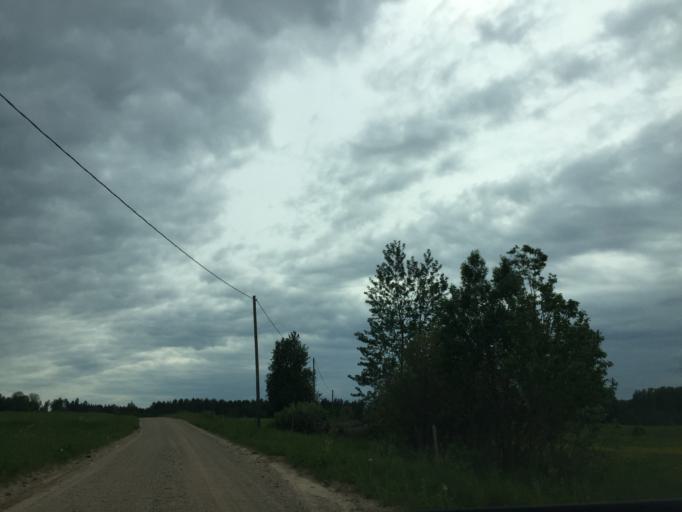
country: LV
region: Aglona
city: Aglona
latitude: 56.1557
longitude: 27.2276
